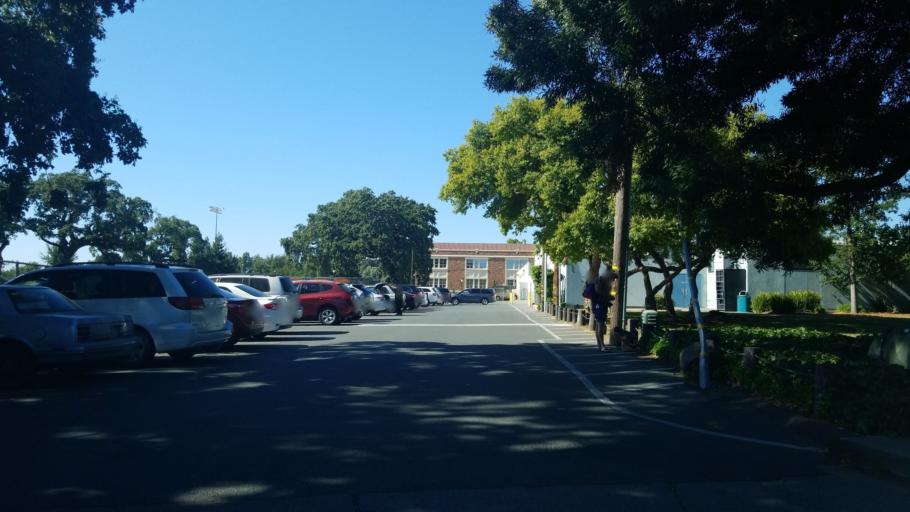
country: US
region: California
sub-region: Sonoma County
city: Santa Rosa
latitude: 38.4498
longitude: -122.7203
